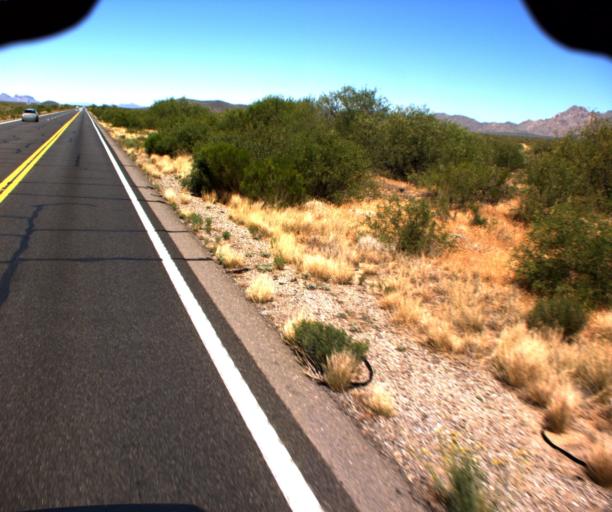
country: US
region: Arizona
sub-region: Yavapai County
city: Congress
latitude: 34.1443
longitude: -112.9805
